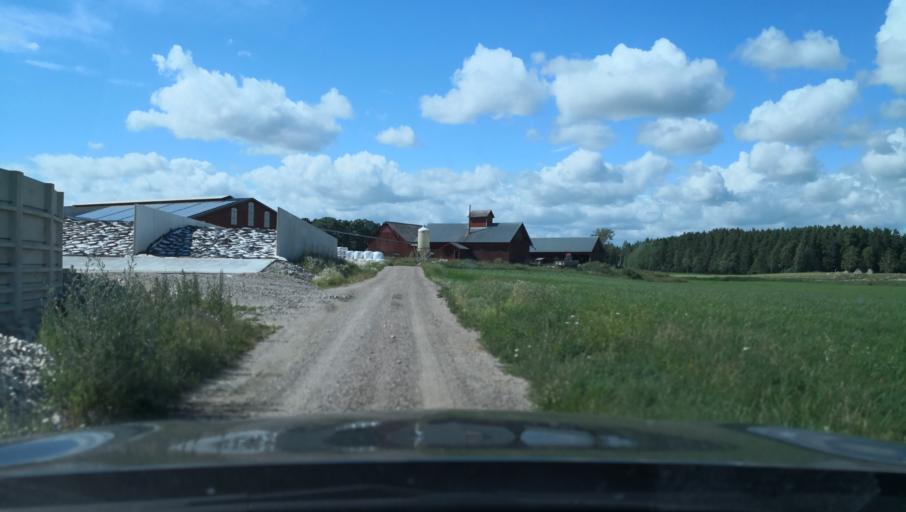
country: SE
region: Vaestmanland
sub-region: Kungsors Kommun
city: Kungsoer
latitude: 59.3204
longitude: 16.0633
